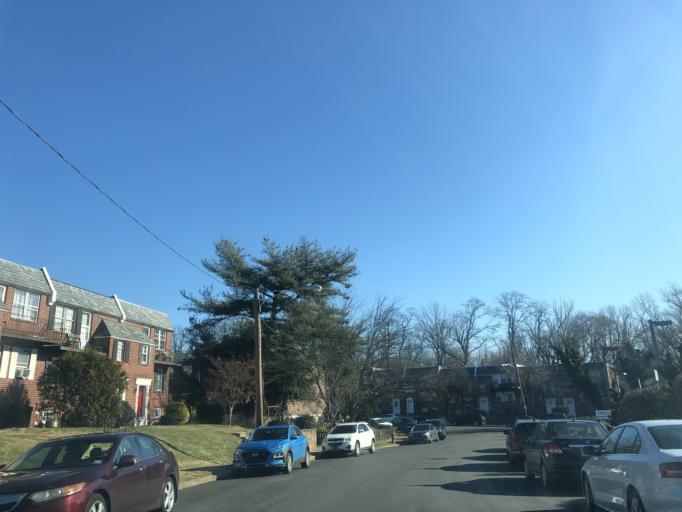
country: US
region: Pennsylvania
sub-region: Montgomery County
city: Bala-Cynwyd
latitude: 40.0004
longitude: -75.2076
